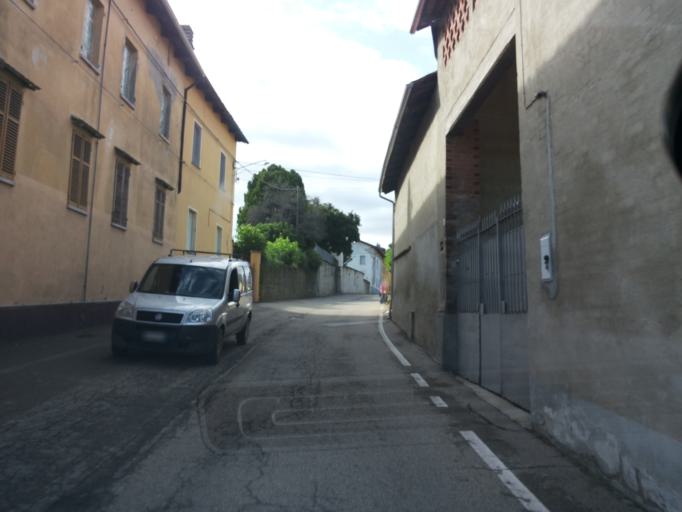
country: IT
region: Piedmont
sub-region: Provincia di Vercelli
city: Moncrivello
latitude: 45.3289
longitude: 8.0019
